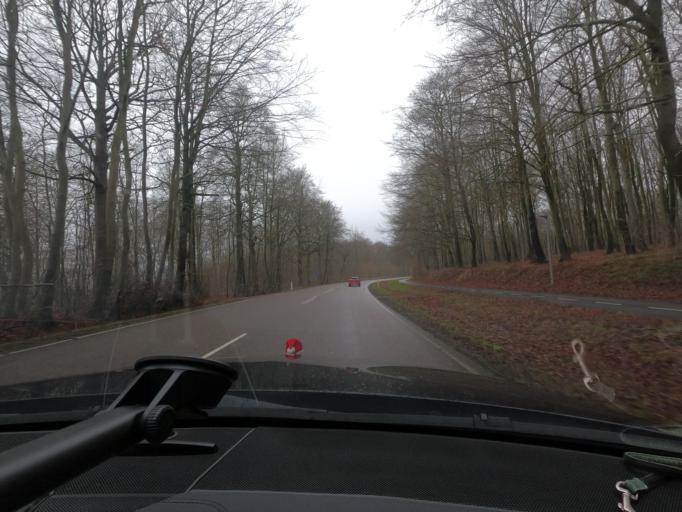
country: DK
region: South Denmark
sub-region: Sonderborg Kommune
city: Horuphav
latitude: 54.9072
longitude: 9.8850
